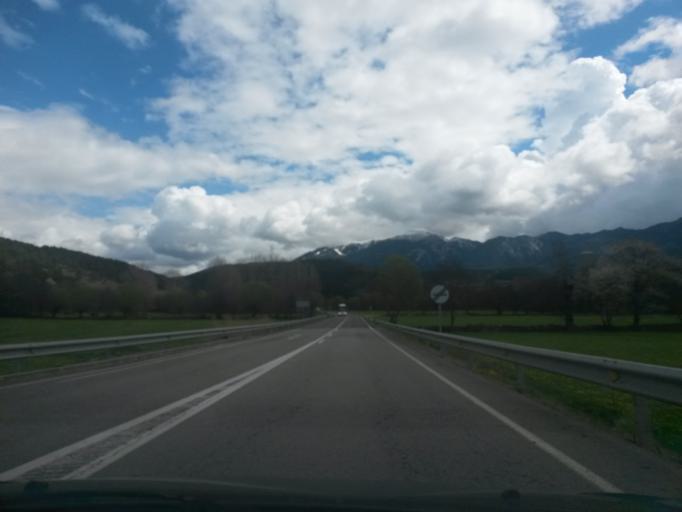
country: ES
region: Catalonia
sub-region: Provincia de Lleida
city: Bellver de Cerdanya
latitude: 42.3730
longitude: 1.7897
